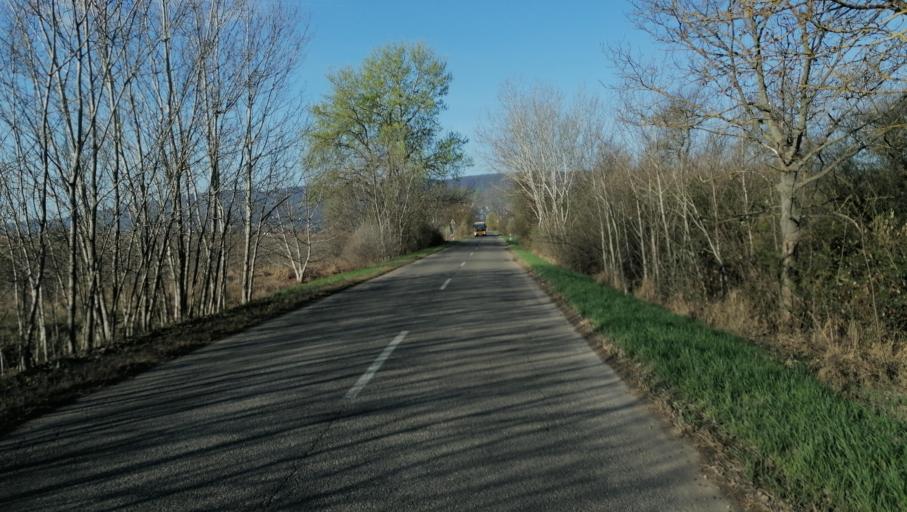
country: HU
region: Pest
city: Tahitotfalu
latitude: 47.7657
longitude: 19.1084
